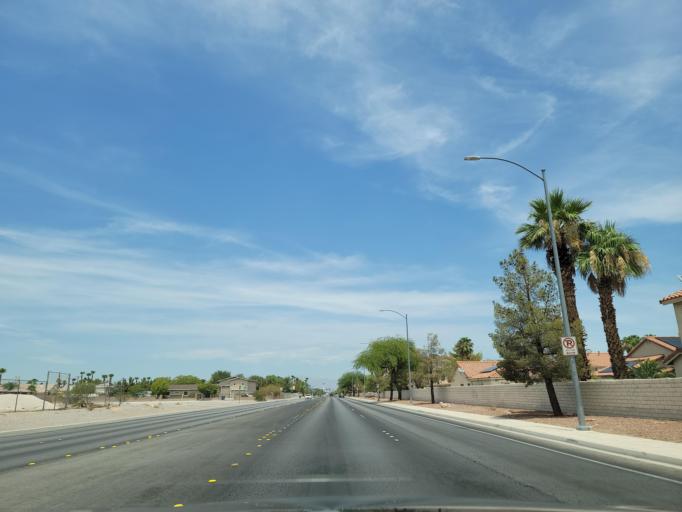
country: US
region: Nevada
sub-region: Clark County
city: Paradise
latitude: 36.0373
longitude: -115.1544
